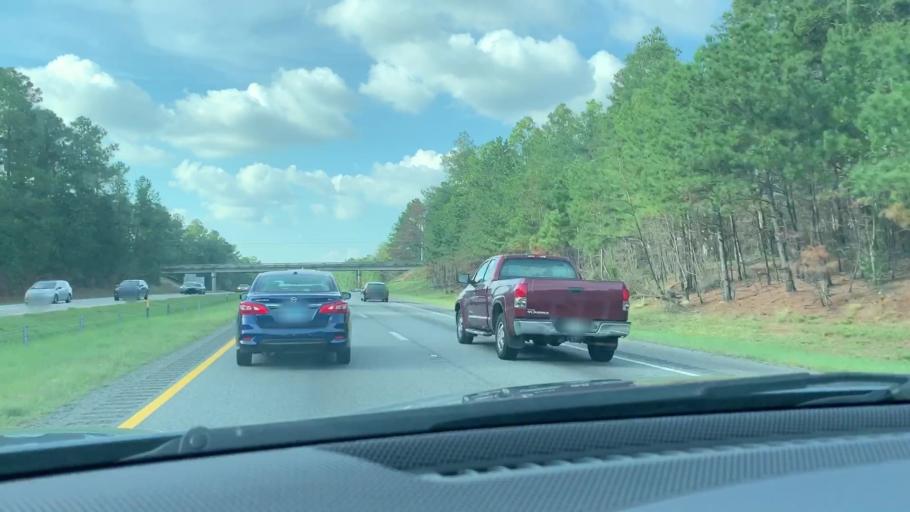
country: US
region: South Carolina
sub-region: Calhoun County
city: Saint Matthews
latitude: 33.6493
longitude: -80.8828
